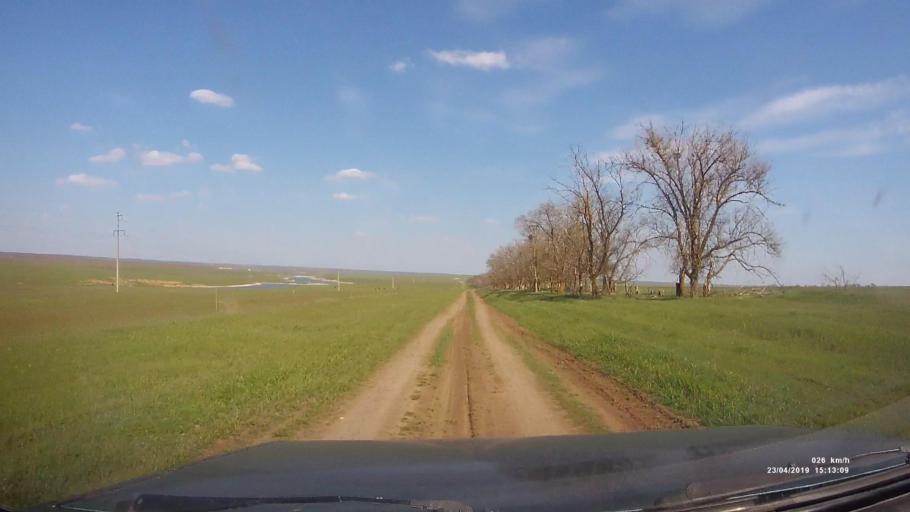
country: RU
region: Rostov
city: Remontnoye
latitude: 46.5398
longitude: 42.9542
